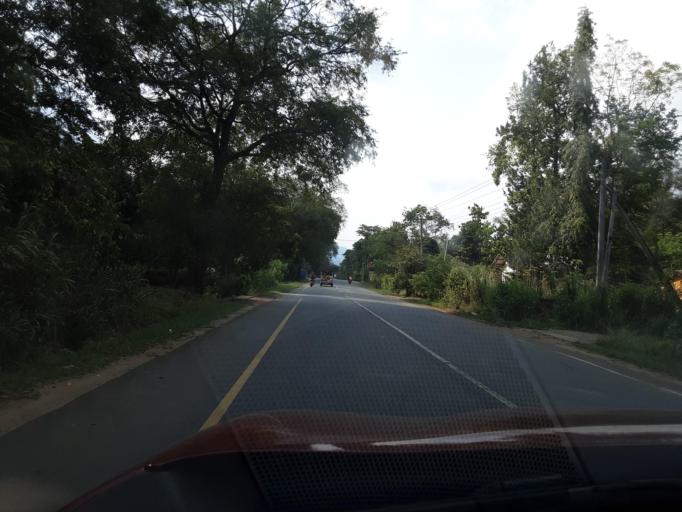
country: LK
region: Uva
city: Haputale
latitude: 6.6807
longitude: 81.1101
